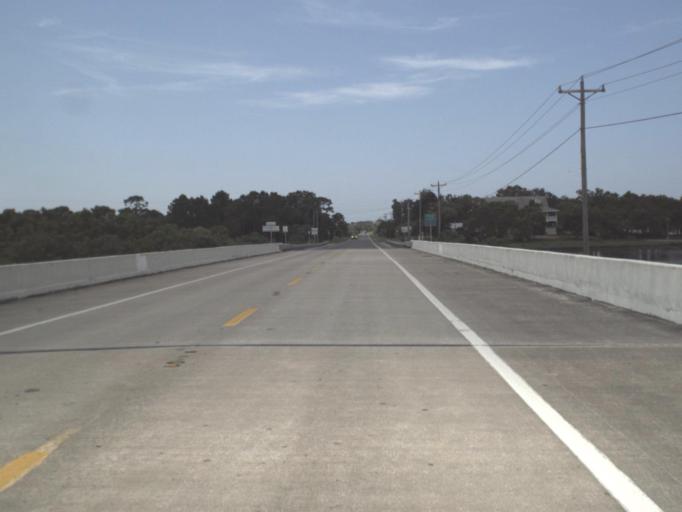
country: US
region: Florida
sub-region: Levy County
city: Chiefland
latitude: 29.1653
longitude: -83.0275
